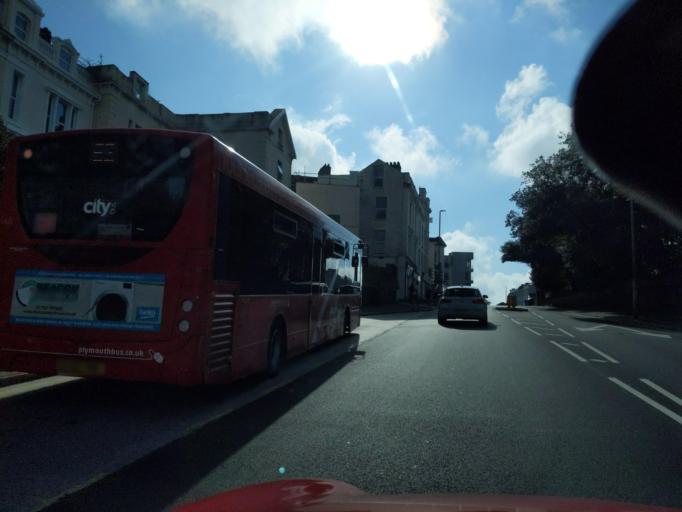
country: GB
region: England
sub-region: Plymouth
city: Plymouth
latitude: 50.3798
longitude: -4.1339
